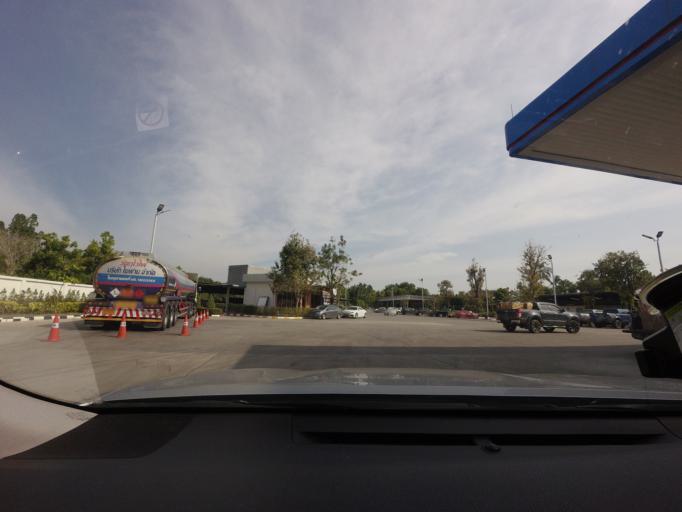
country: TH
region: Narathiwat
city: Narathiwat
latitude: 6.3863
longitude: 101.8112
